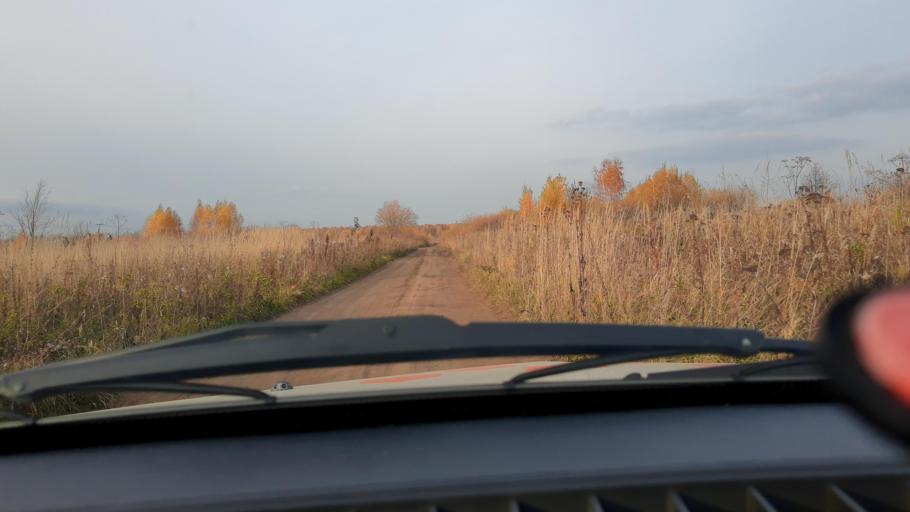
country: RU
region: Bashkortostan
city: Iglino
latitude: 54.7995
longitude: 56.3463
